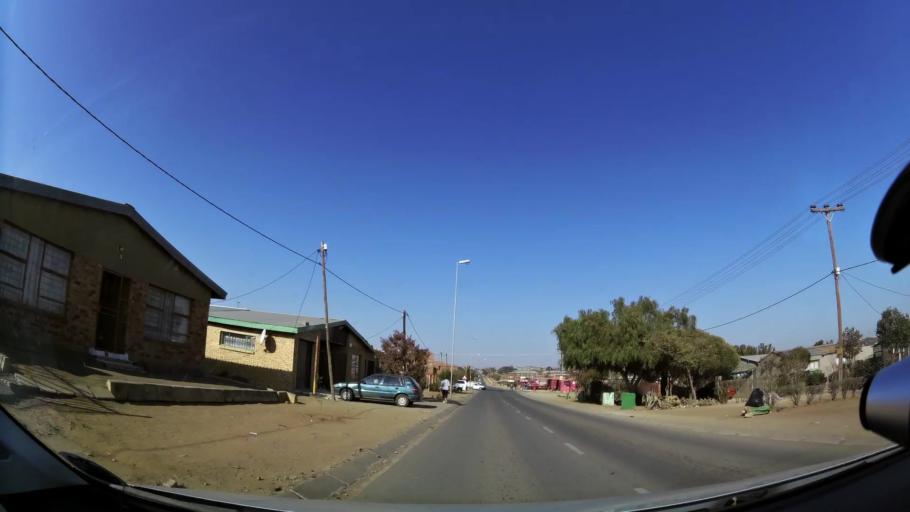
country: ZA
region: Orange Free State
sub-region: Mangaung Metropolitan Municipality
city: Bloemfontein
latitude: -29.1796
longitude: 26.2244
